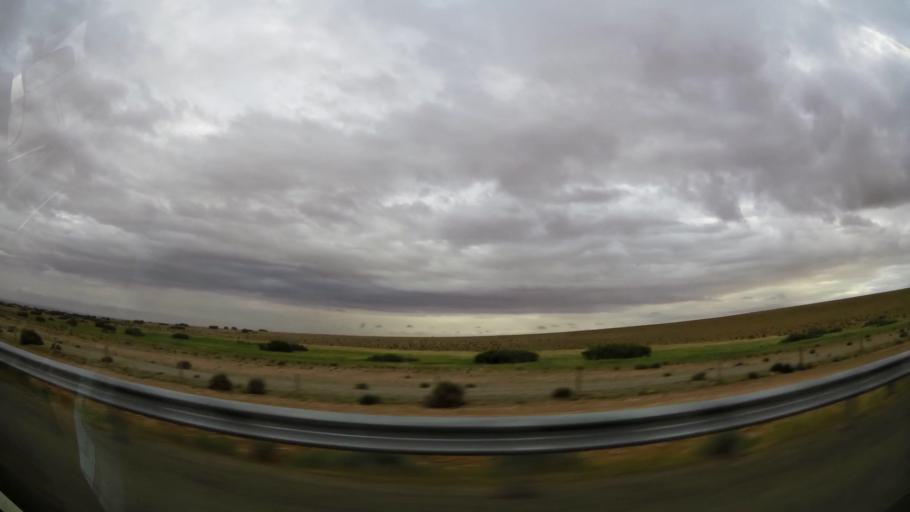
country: MA
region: Taza-Al Hoceima-Taounate
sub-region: Taza
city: Guercif
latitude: 34.3053
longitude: -3.6493
